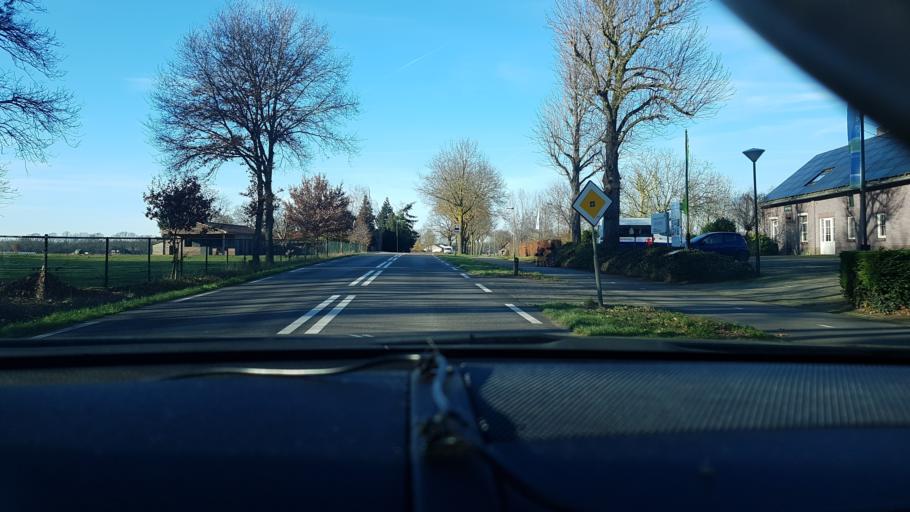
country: NL
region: Limburg
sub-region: Gemeente Beesel
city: Beesel
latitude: 51.2980
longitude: 6.0373
